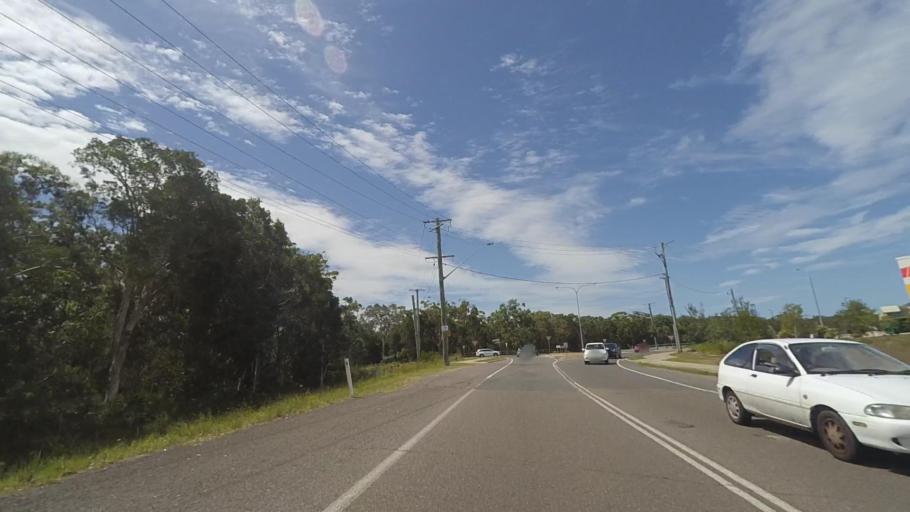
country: AU
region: New South Wales
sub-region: Port Stephens Shire
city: Anna Bay
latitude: -32.7500
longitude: 152.0684
